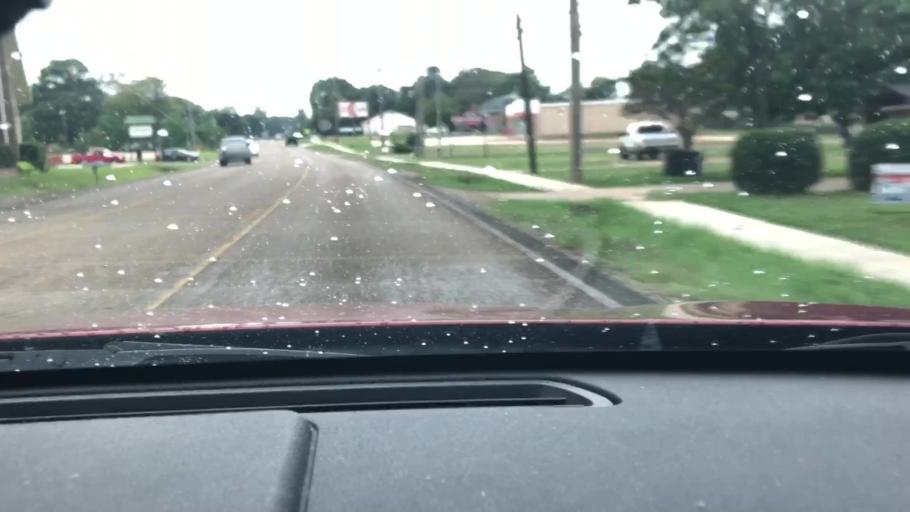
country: US
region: Texas
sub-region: Bowie County
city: Nash
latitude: 33.4428
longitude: -94.1218
